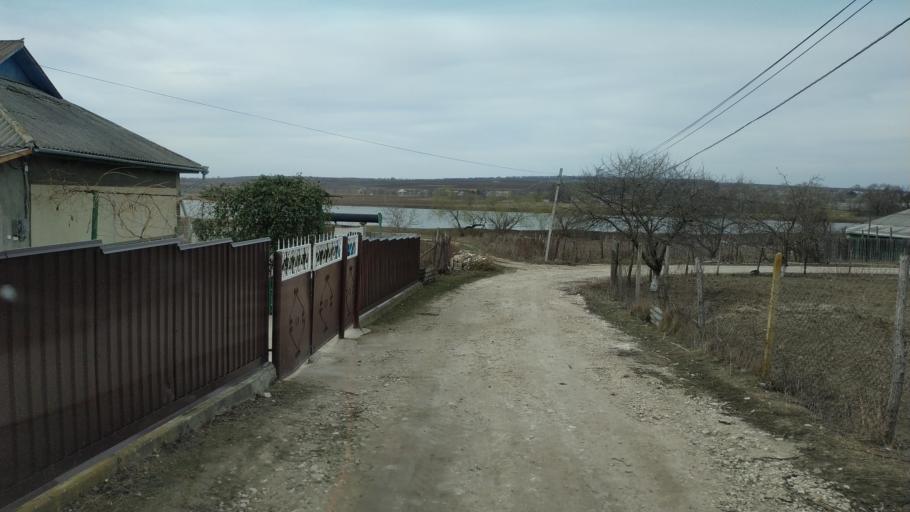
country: MD
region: Hincesti
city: Dancu
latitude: 46.8528
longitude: 28.2524
